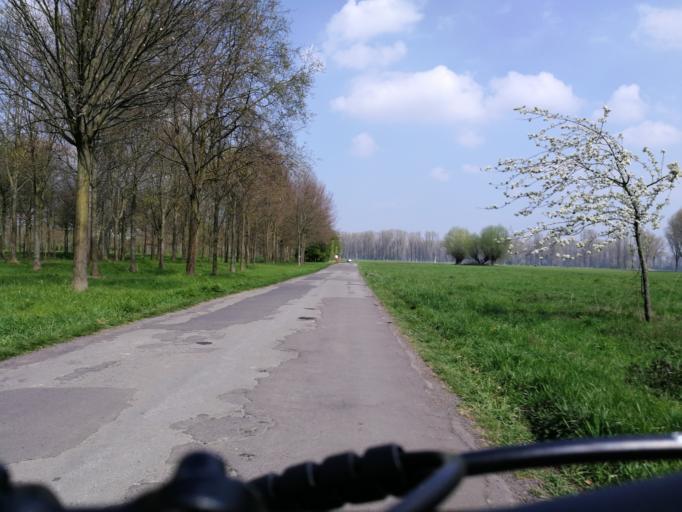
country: DE
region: North Rhine-Westphalia
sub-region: Regierungsbezirk Dusseldorf
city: Dormagen
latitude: 51.1447
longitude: 6.8268
